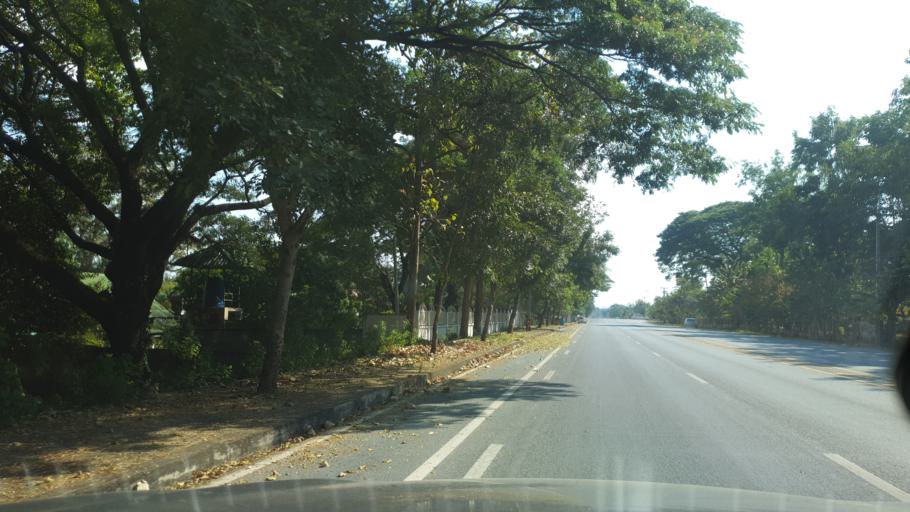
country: TH
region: Tak
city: Tak
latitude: 16.8685
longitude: 99.1193
